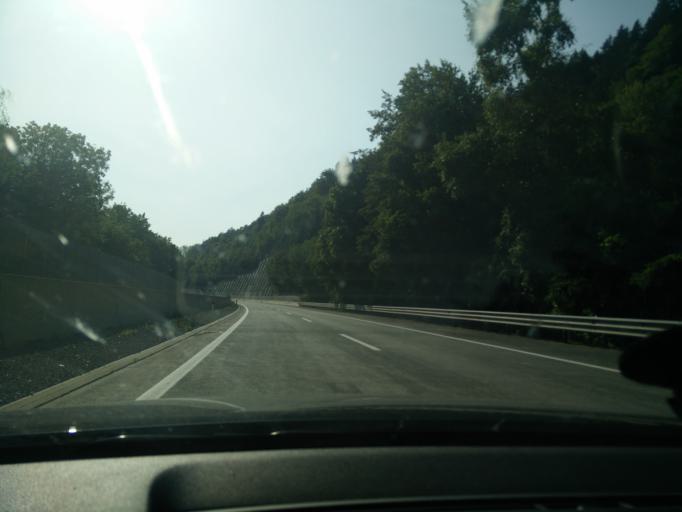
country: AT
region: Carinthia
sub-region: Politischer Bezirk Klagenfurt Land
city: Maria Worth
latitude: 46.6396
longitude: 14.1522
